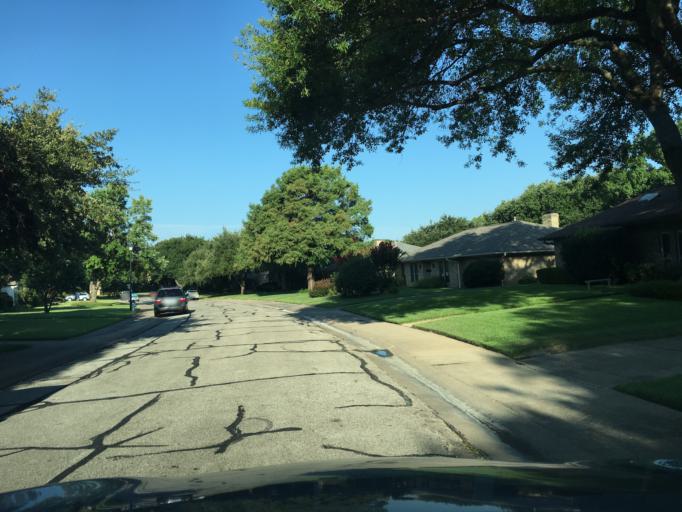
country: US
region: Texas
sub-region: Dallas County
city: Addison
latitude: 32.9651
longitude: -96.8573
